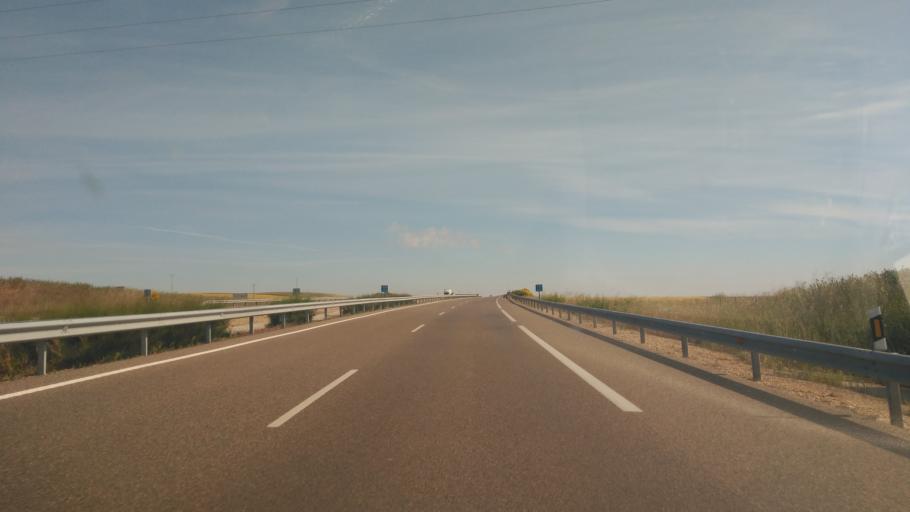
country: ES
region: Castille and Leon
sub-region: Provincia de Zamora
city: Cazurra
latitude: 41.3982
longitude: -5.7180
